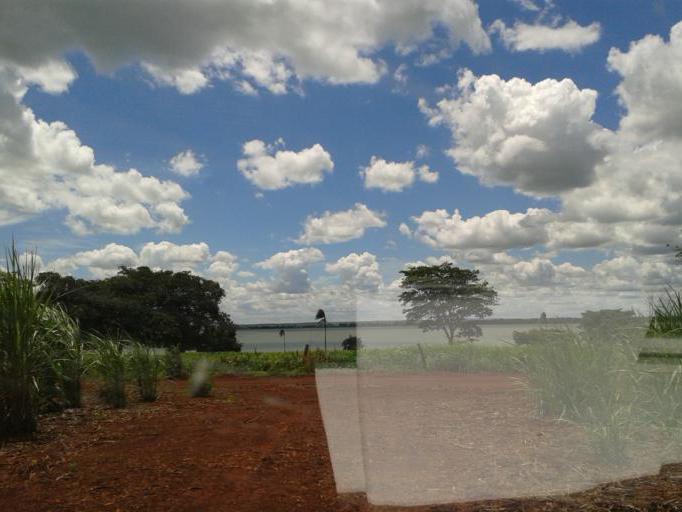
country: BR
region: Minas Gerais
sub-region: Santa Vitoria
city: Santa Vitoria
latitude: -18.6903
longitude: -50.1935
